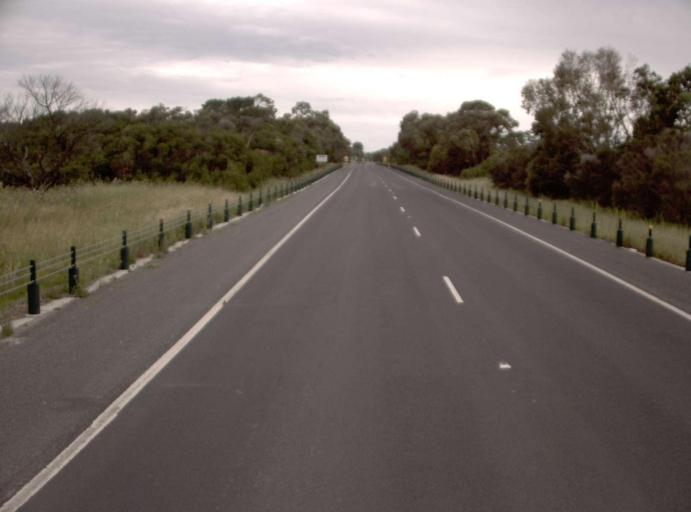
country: AU
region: Victoria
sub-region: Casey
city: Blind Bight
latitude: -38.1874
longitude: 145.3456
